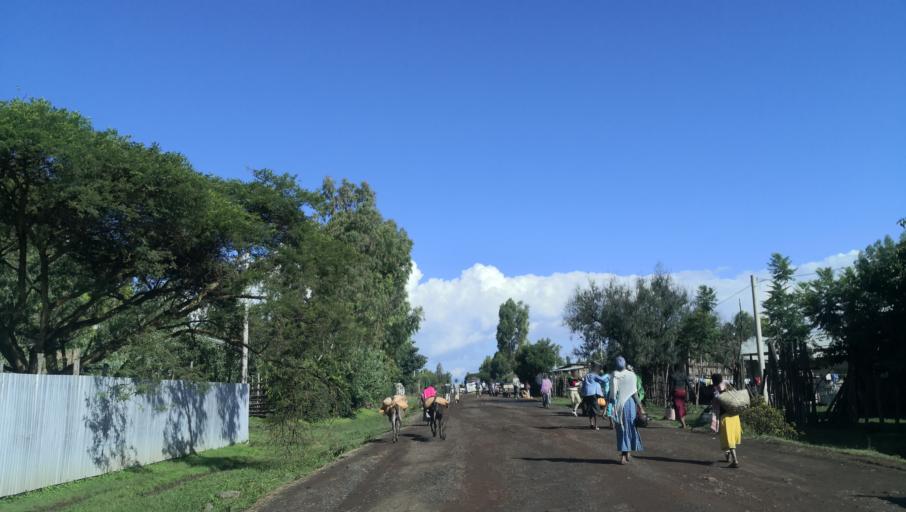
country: ET
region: Oromiya
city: Tulu Bolo
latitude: 8.6459
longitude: 38.2205
